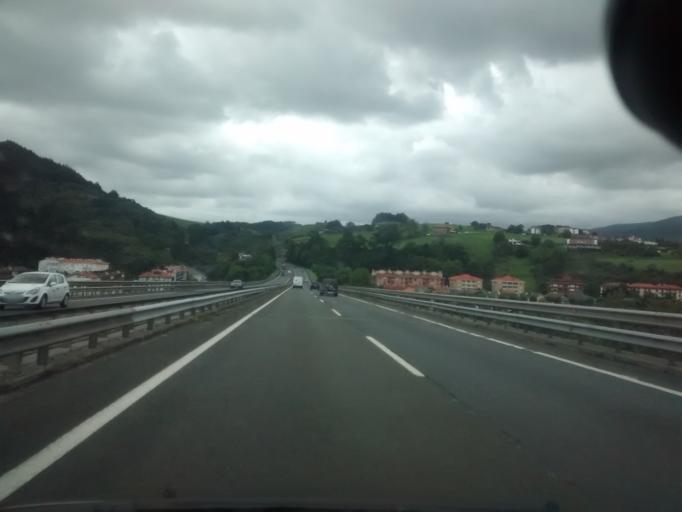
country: ES
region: Basque Country
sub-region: Provincia de Guipuzcoa
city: Orio
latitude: 43.2828
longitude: -2.1309
